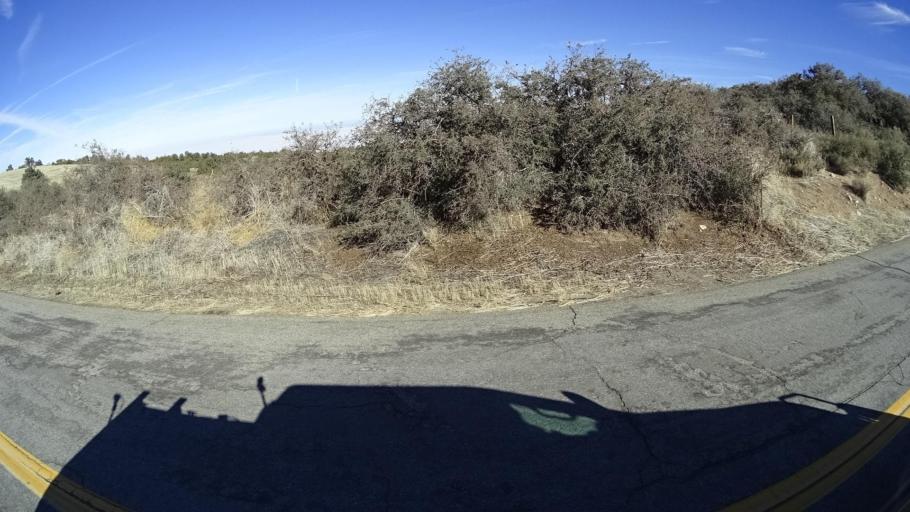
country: US
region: California
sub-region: Kern County
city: Pine Mountain Club
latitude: 34.8689
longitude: -119.3252
